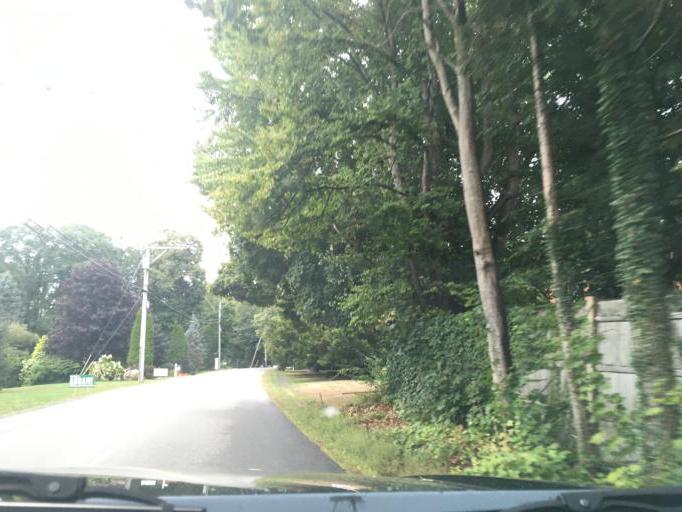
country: US
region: New Hampshire
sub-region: Rockingham County
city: Exeter
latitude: 42.9879
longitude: -70.9053
